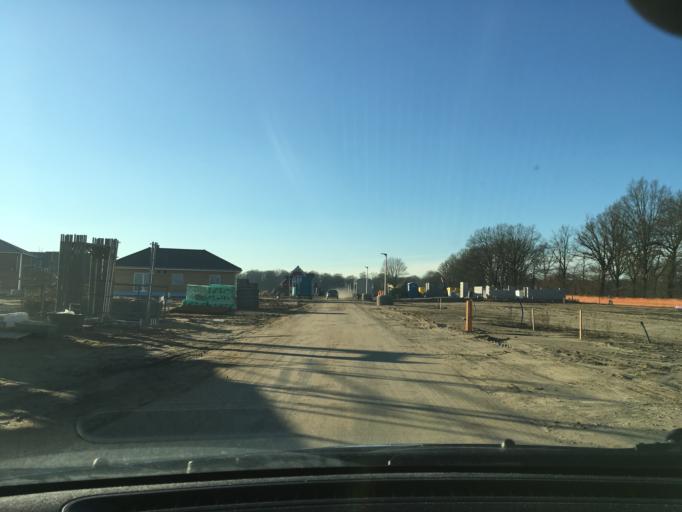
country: DE
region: Schleswig-Holstein
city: Buchen
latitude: 53.4773
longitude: 10.5995
